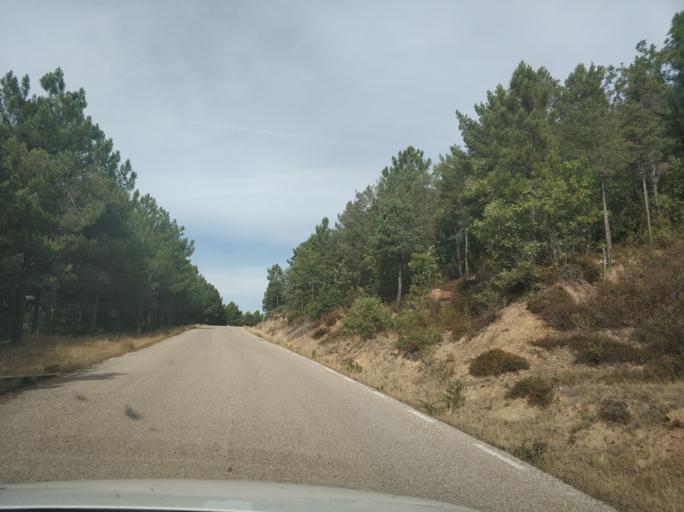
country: ES
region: Castille and Leon
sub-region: Provincia de Soria
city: Duruelo de la Sierra
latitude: 41.9008
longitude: -2.9394
